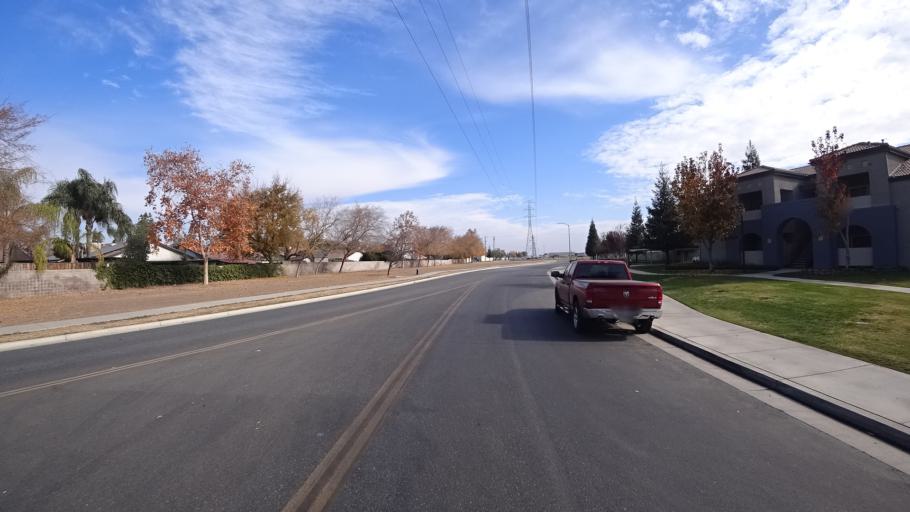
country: US
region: California
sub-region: Kern County
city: Greenacres
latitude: 35.3976
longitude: -119.0852
